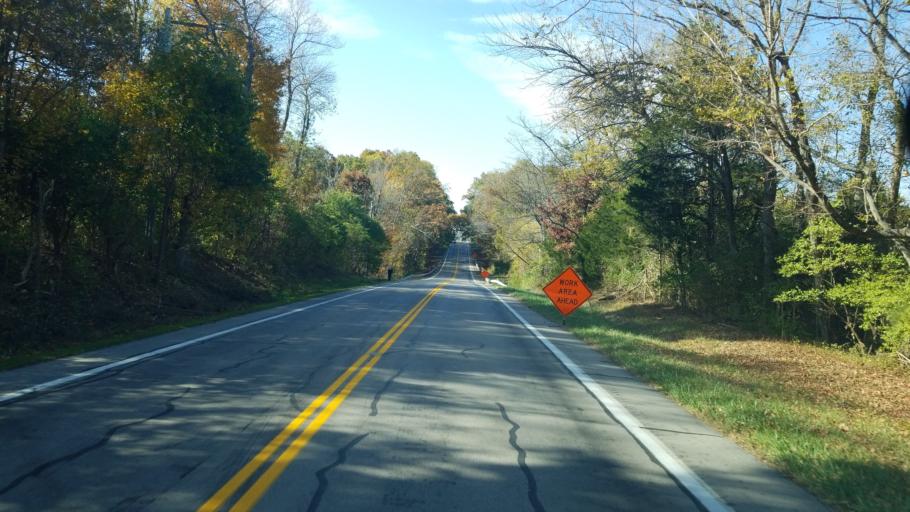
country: US
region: Ohio
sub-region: Warren County
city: Morrow
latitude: 39.3775
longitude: -84.0506
